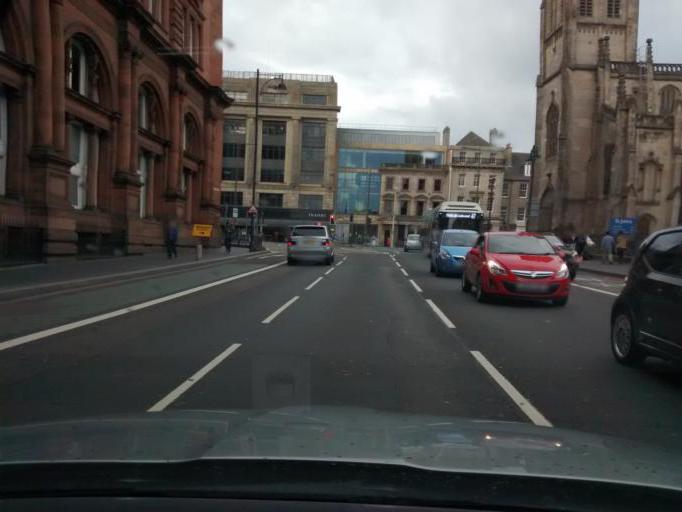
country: GB
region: Scotland
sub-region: Edinburgh
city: Edinburgh
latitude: 55.9494
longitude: -3.2068
